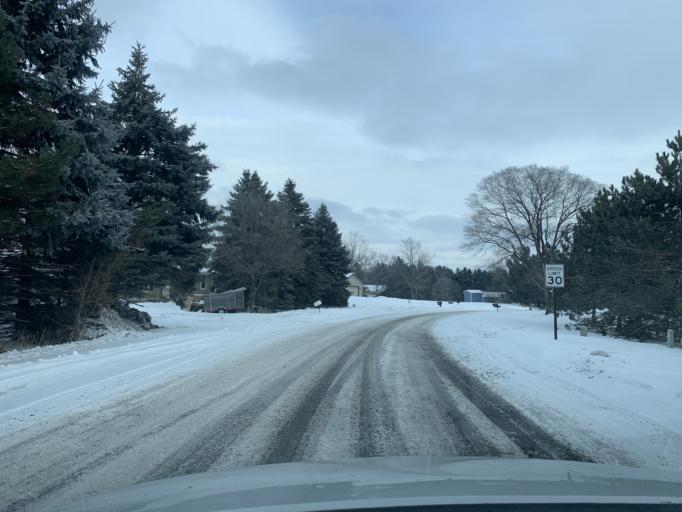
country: US
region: Minnesota
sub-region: Anoka County
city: Ramsey
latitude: 45.2435
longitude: -93.4121
